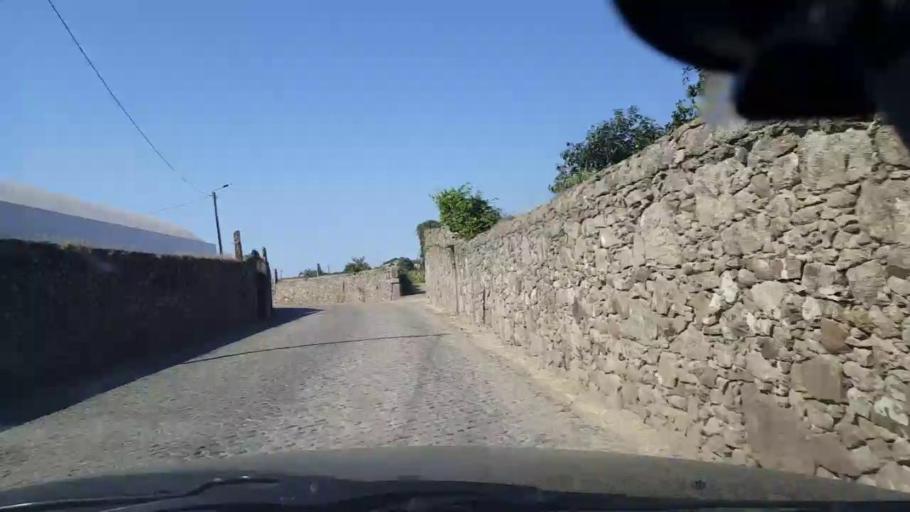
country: PT
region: Porto
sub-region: Povoa de Varzim
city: Pedroso
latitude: 41.4014
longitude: -8.6909
